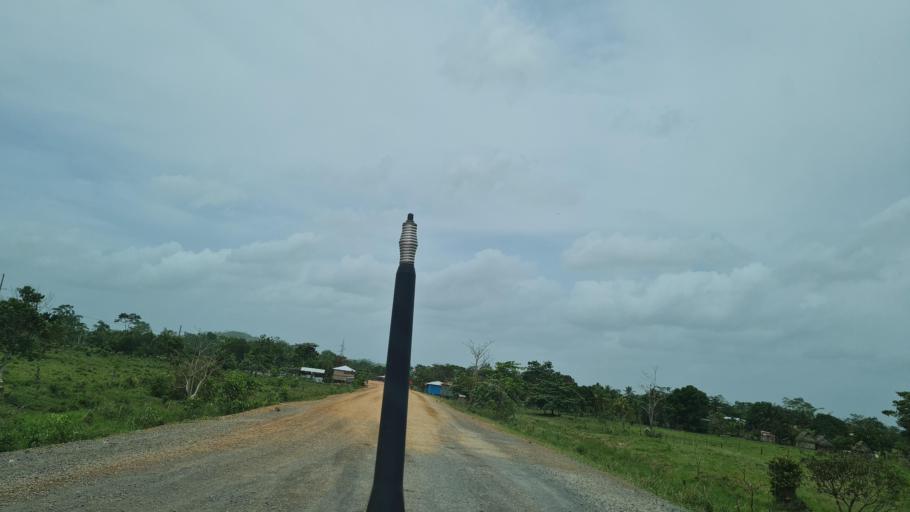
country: NI
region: Atlantico Norte (RAAN)
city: Bonanza
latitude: 14.0406
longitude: -84.0752
